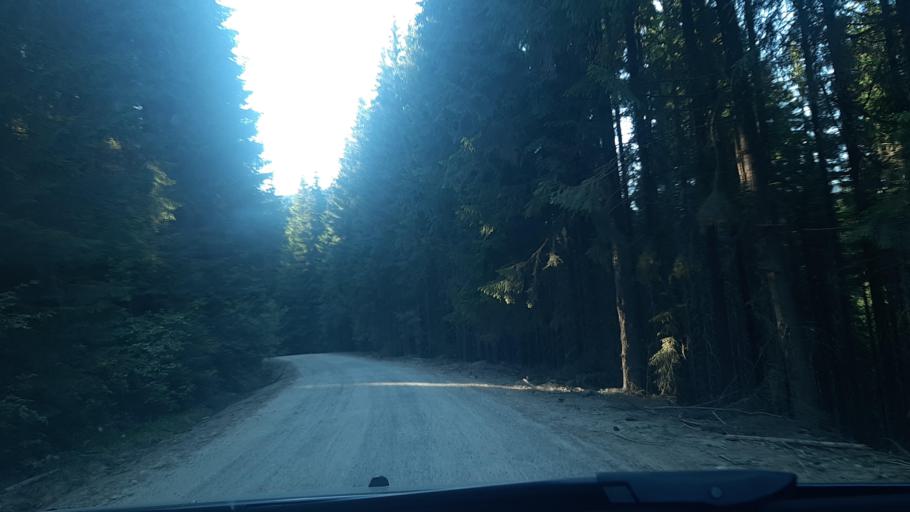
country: RO
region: Alba
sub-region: Comuna Sugag
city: Sugag
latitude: 45.5778
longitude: 23.6093
